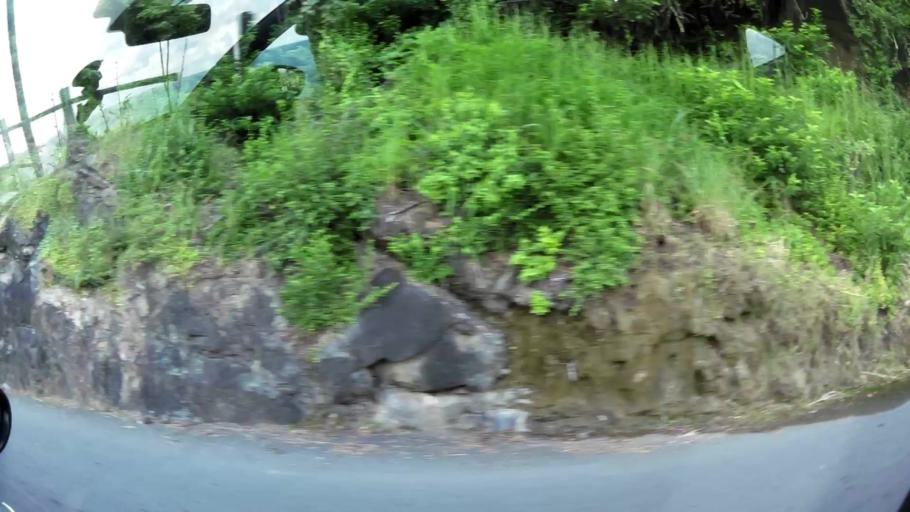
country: TT
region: Eastern Tobago
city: Roxborough
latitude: 11.2347
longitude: -60.5958
